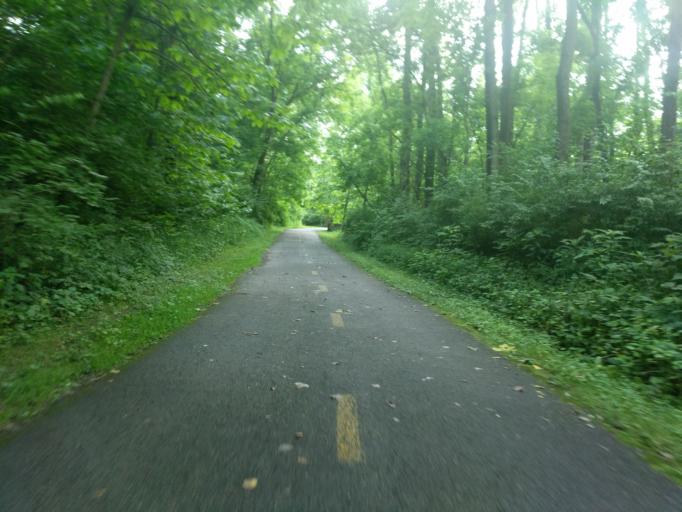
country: US
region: Ohio
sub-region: Franklin County
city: Huber Ridge
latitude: 40.0778
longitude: -82.9195
